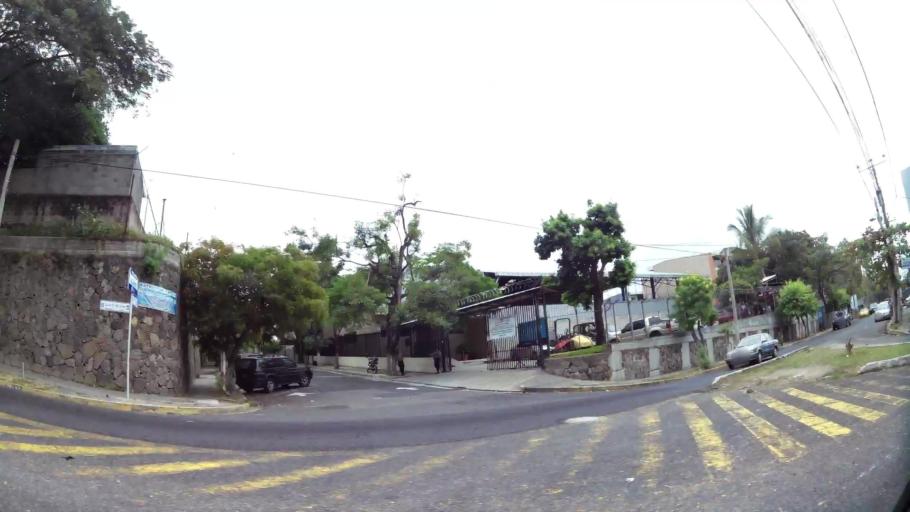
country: SV
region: San Salvador
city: Mejicanos
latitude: 13.7086
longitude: -89.2390
